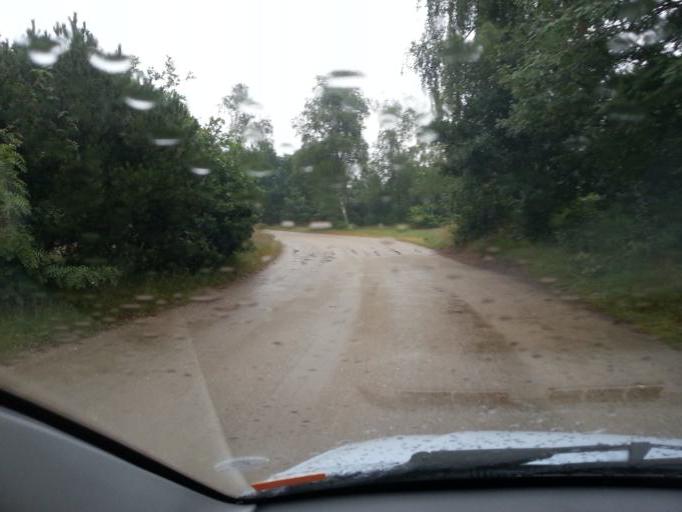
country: DK
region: South Denmark
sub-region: Vejle Kommune
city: Jelling
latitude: 55.8075
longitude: 9.3518
